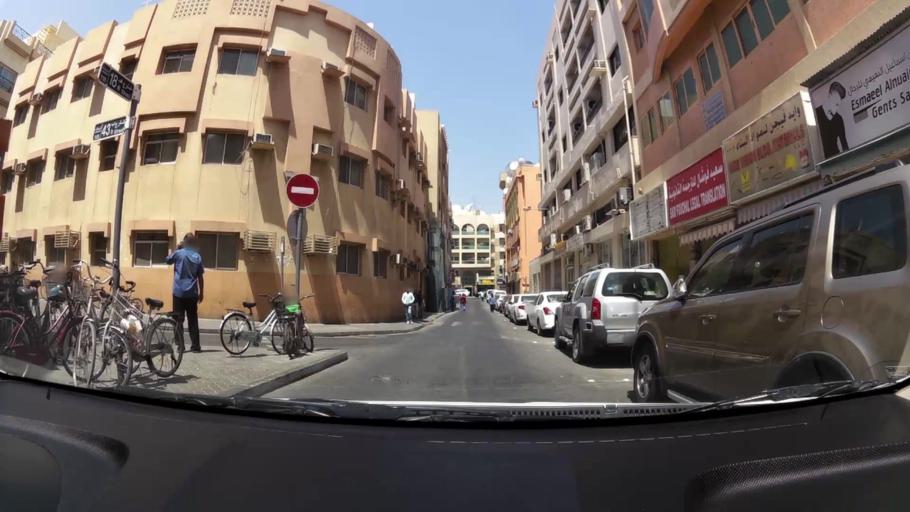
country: AE
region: Ash Shariqah
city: Sharjah
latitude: 25.2735
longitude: 55.3144
